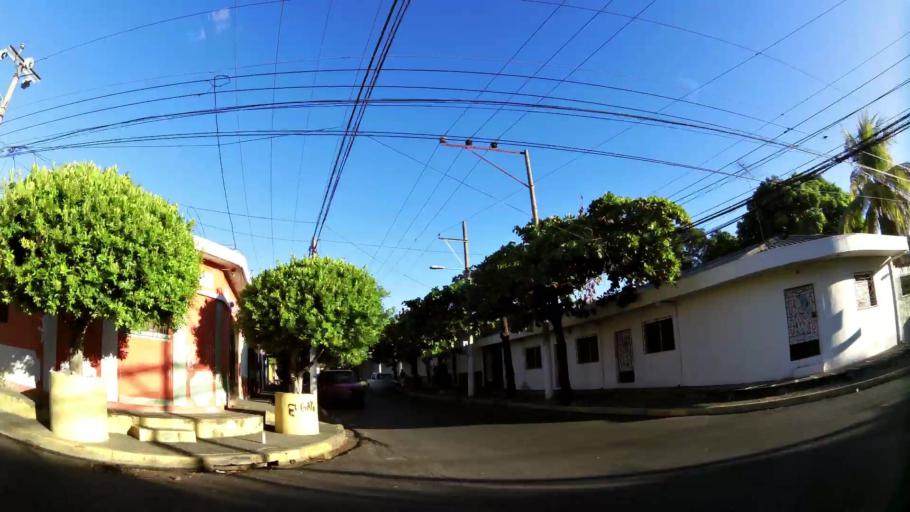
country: SV
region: San Miguel
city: San Miguel
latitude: 13.4868
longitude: -88.1832
